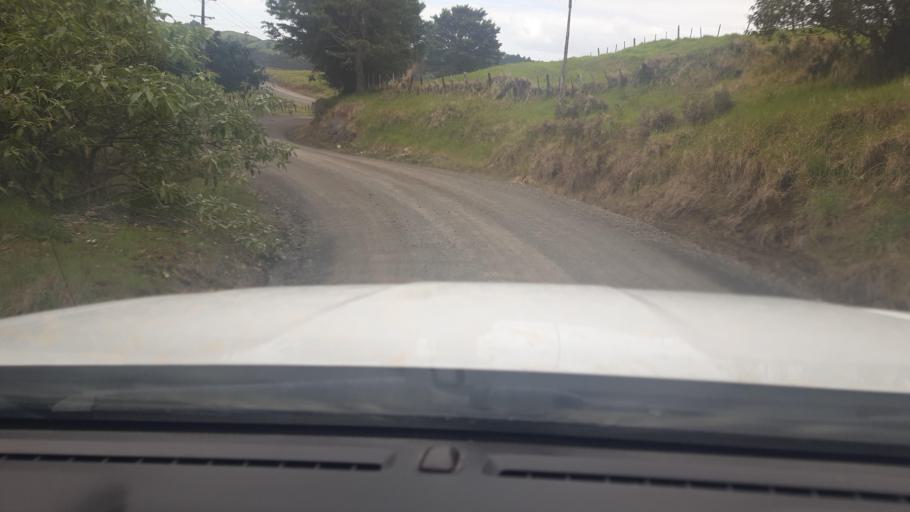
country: NZ
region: Northland
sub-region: Far North District
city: Kaitaia
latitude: -35.0870
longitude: 173.3210
